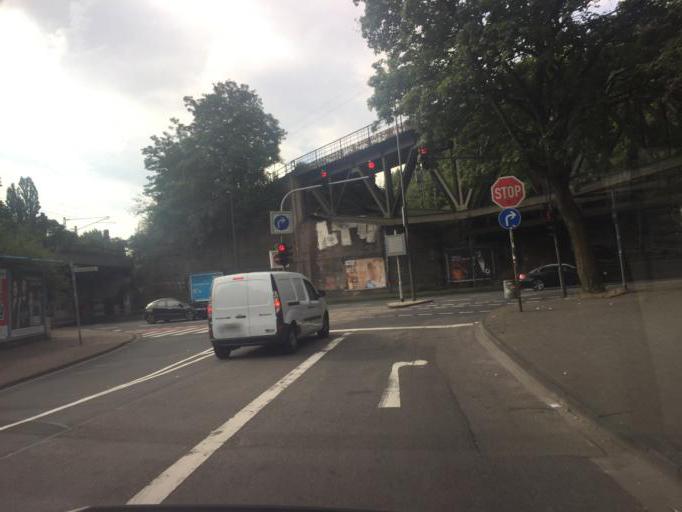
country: DE
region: North Rhine-Westphalia
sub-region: Regierungsbezirk Koln
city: Neuehrenfeld
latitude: 50.9541
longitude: 6.9408
